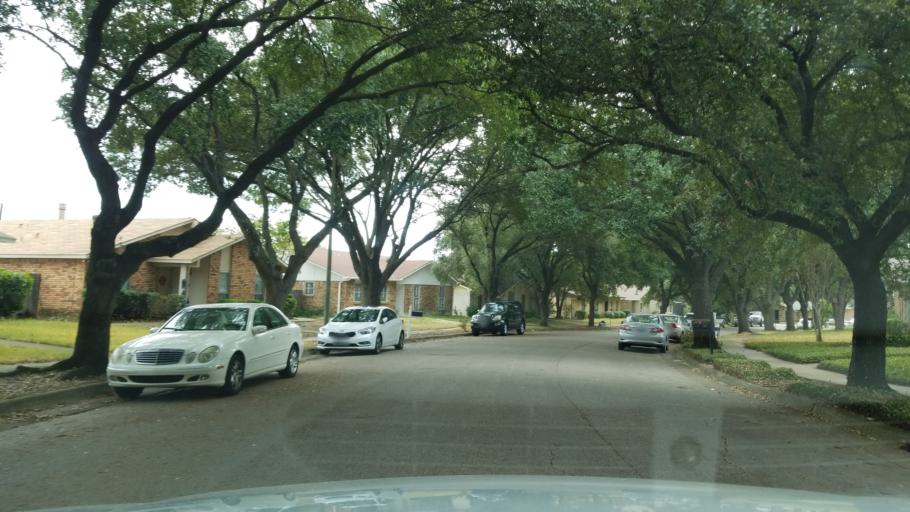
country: US
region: Texas
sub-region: Dallas County
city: Garland
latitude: 32.8766
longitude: -96.6936
